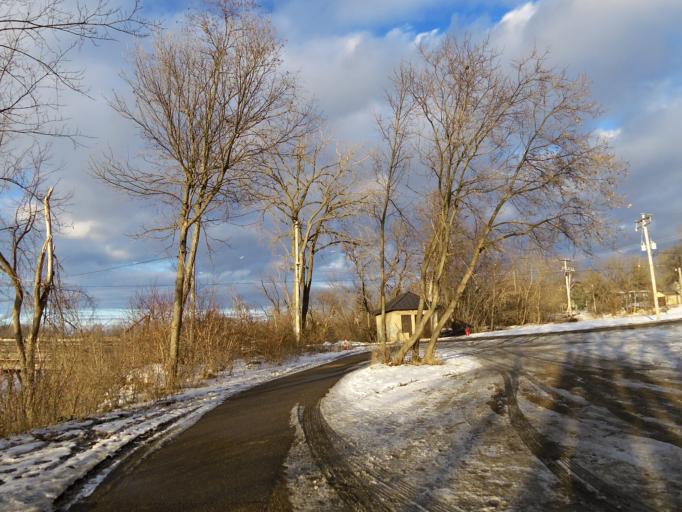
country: US
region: Wisconsin
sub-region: Saint Croix County
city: Hudson
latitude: 44.9822
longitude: -92.7608
